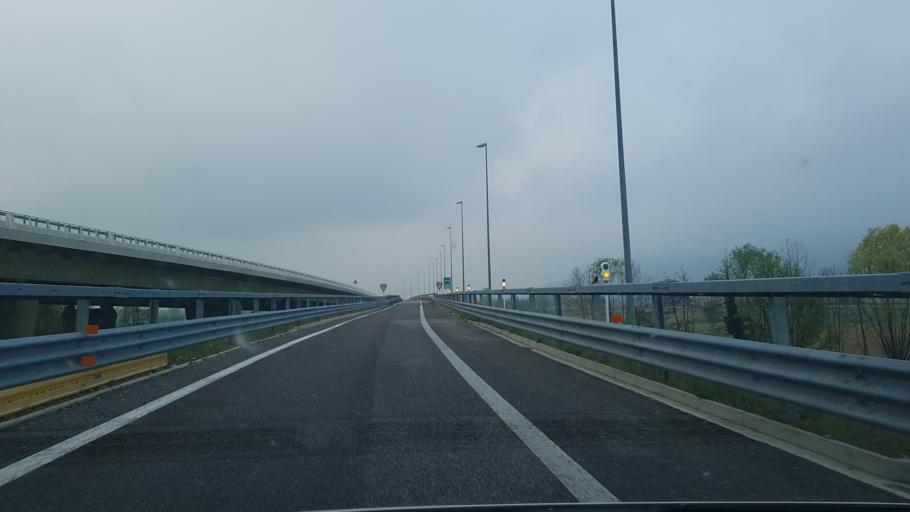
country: IT
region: Veneto
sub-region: Provincia di Vicenza
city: Torri di Quartesolo
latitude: 45.5049
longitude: 11.6161
